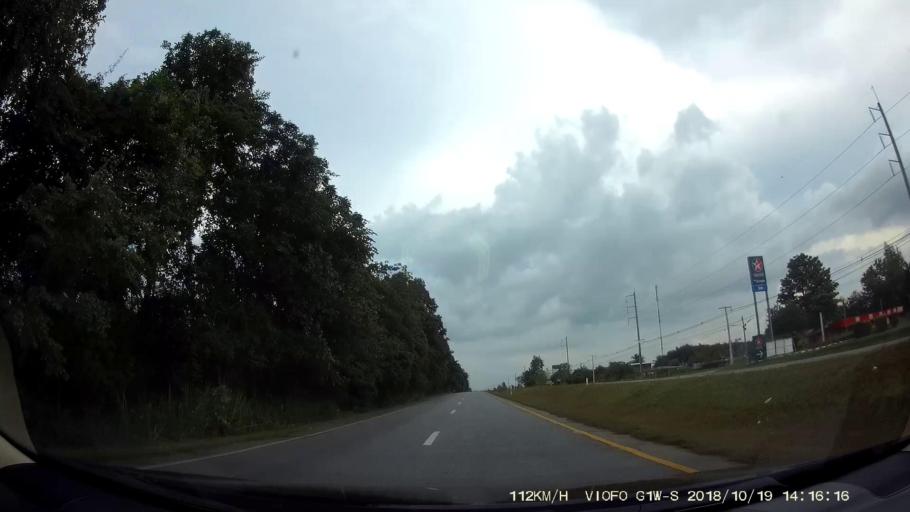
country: TH
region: Chaiyaphum
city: Khon Sawan
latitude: 15.9920
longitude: 102.2093
